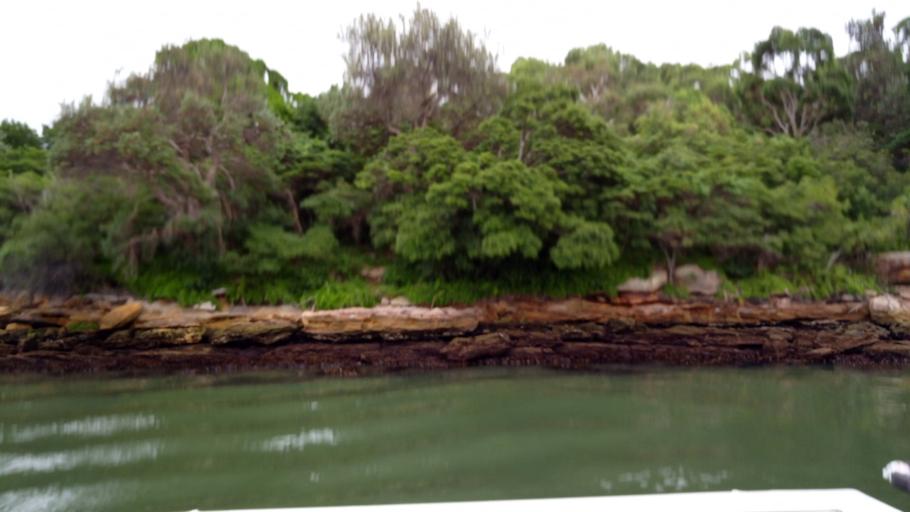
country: AU
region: New South Wales
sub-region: Hunters Hill
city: Hunters Hill
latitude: -33.8423
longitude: 151.1418
